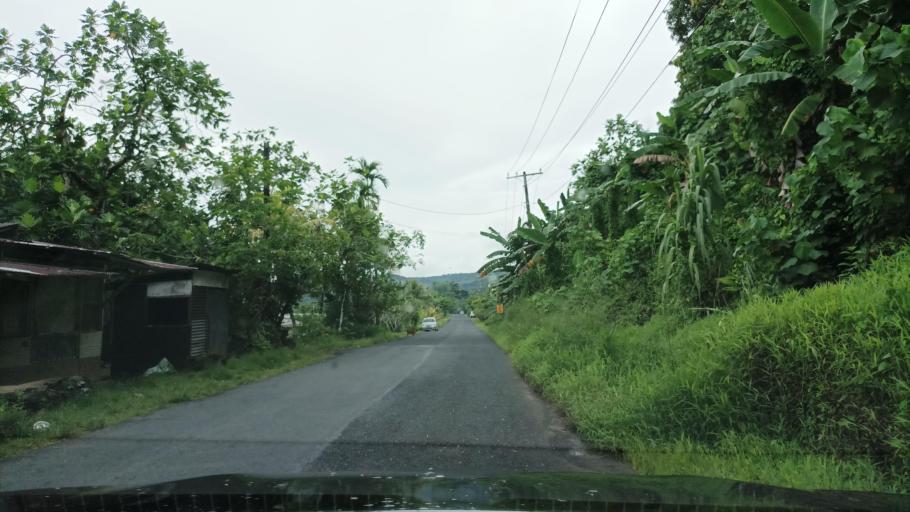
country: FM
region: Pohnpei
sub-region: Kolonia Municipality
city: Kolonia
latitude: 6.9560
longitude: 158.2779
